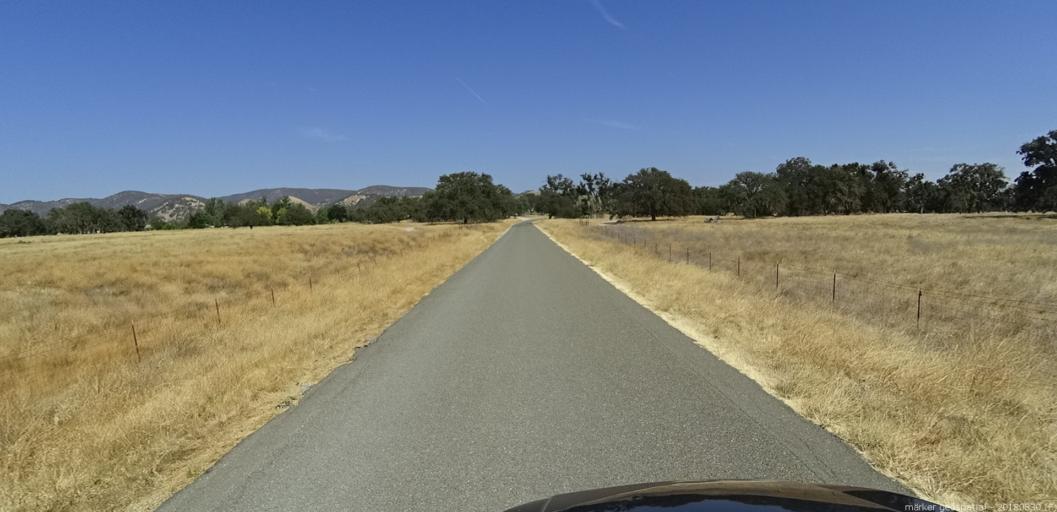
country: US
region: California
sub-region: Monterey County
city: King City
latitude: 36.0249
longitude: -121.1753
